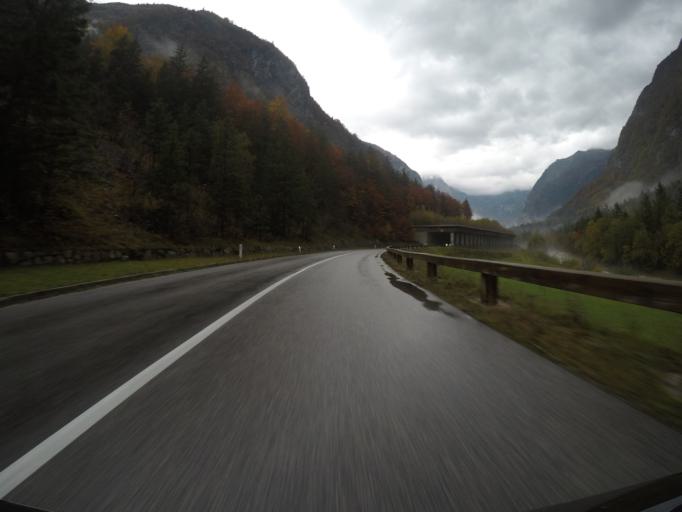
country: SI
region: Kranjska Gora
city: Kranjska Gora
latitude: 46.3635
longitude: 13.7147
